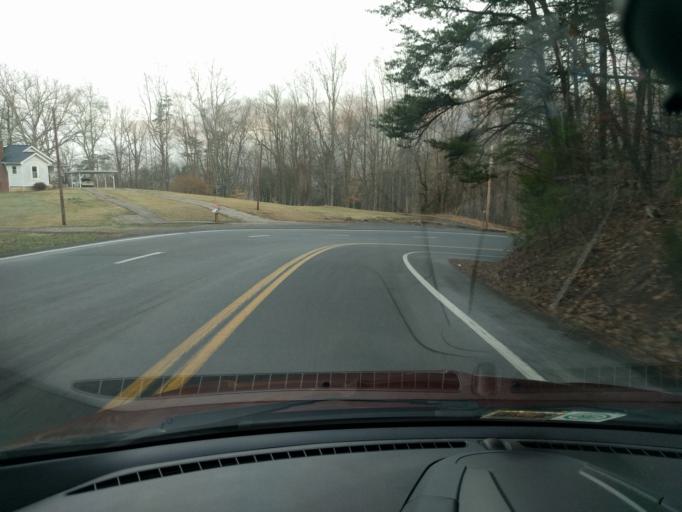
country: US
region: West Virginia
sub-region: Fayette County
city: Ansted
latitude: 38.1326
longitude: -81.1462
